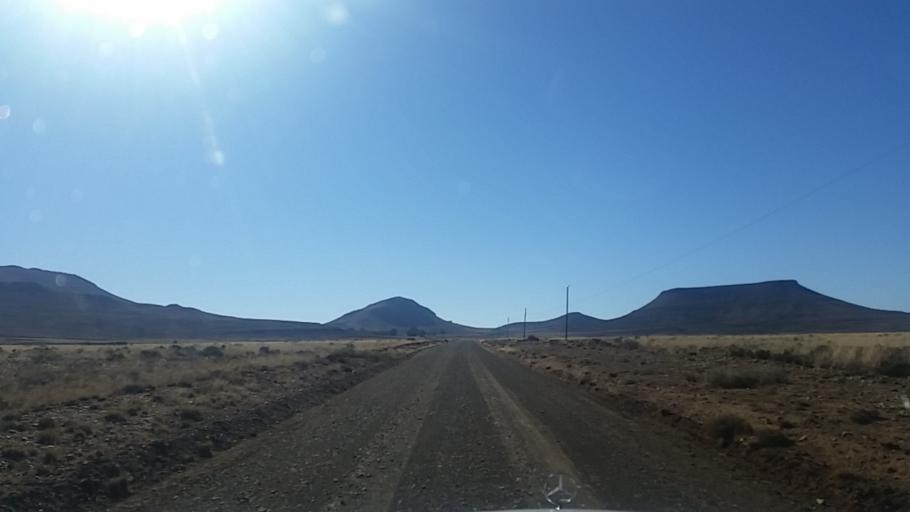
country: ZA
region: Eastern Cape
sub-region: Chris Hani District Municipality
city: Middelburg
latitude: -31.7963
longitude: 24.7077
